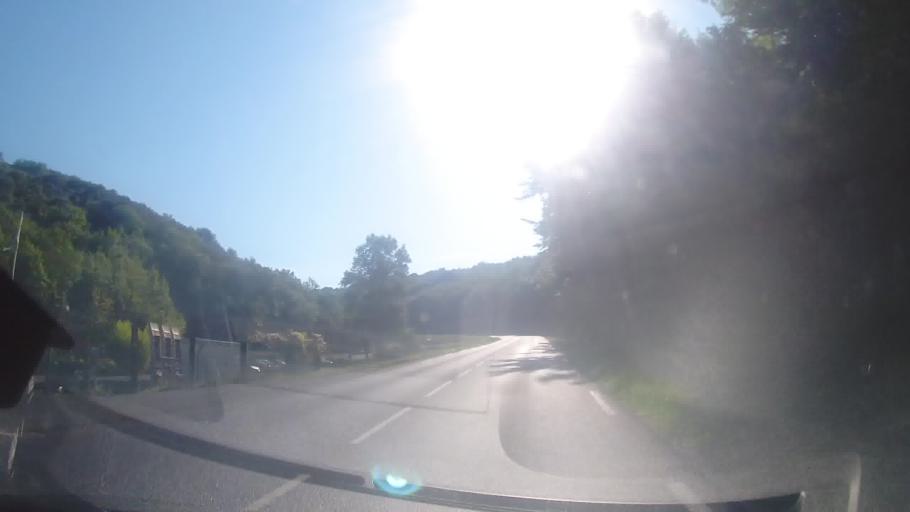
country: FR
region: Aquitaine
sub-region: Departement de la Dordogne
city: Sarlat-la-Caneda
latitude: 44.8535
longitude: 1.1955
